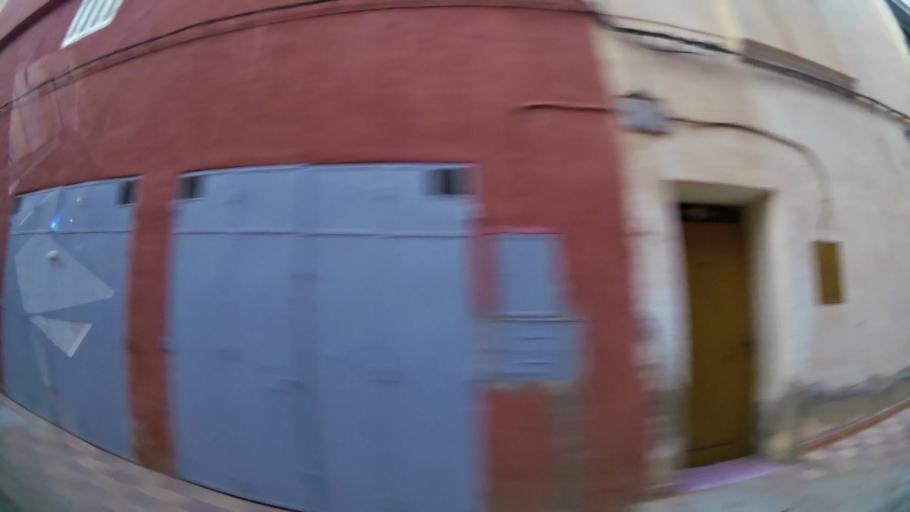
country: MA
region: Oriental
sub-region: Berkane-Taourirt
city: Berkane
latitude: 34.9195
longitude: -2.3197
